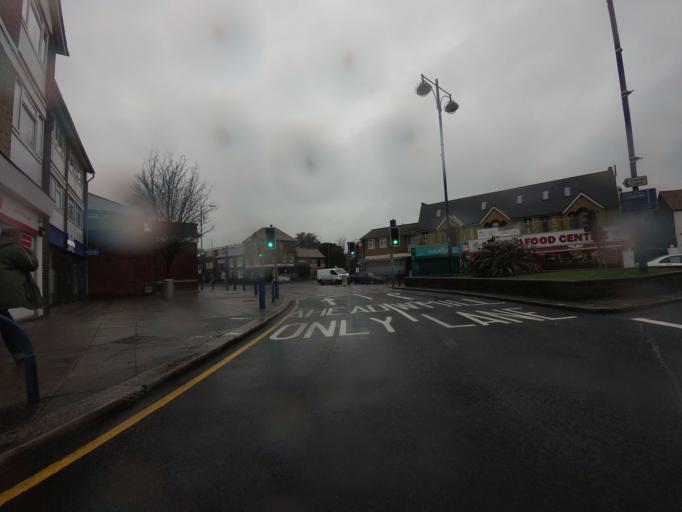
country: GB
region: England
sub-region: Hertfordshire
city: Cheshunt
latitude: 51.7023
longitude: -0.0347
